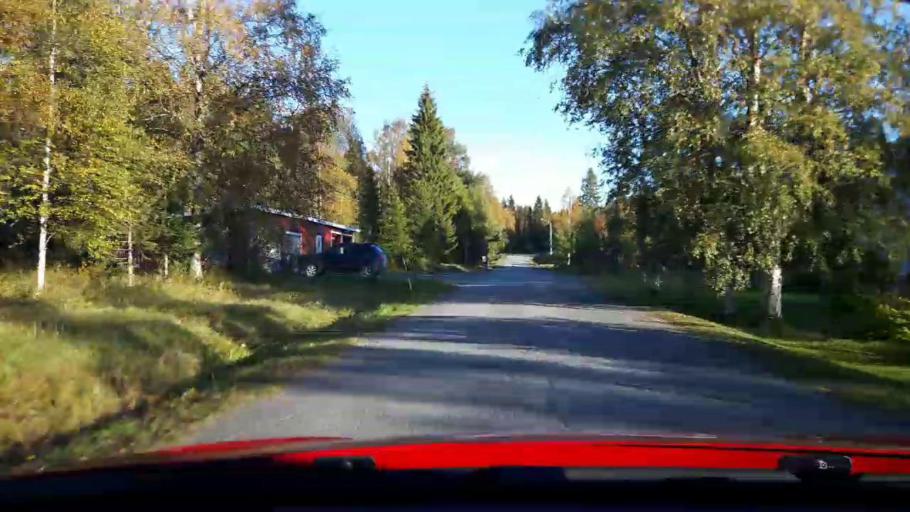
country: SE
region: Jaemtland
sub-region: OEstersunds Kommun
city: Lit
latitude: 63.6095
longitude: 14.7777
